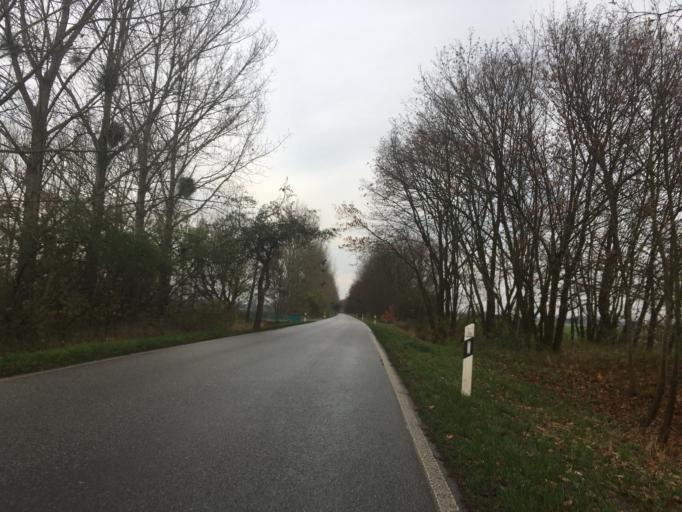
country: DE
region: Brandenburg
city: Letschin
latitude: 52.6847
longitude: 14.4031
